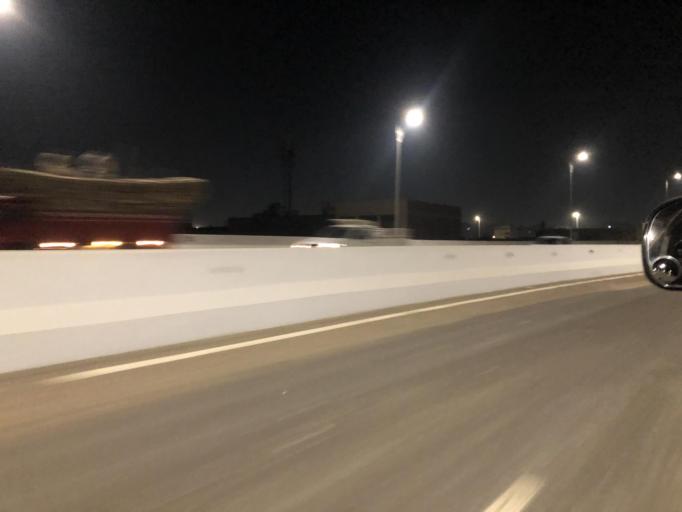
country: EG
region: Al Jizah
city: Al Jizah
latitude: 29.9927
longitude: 31.2603
